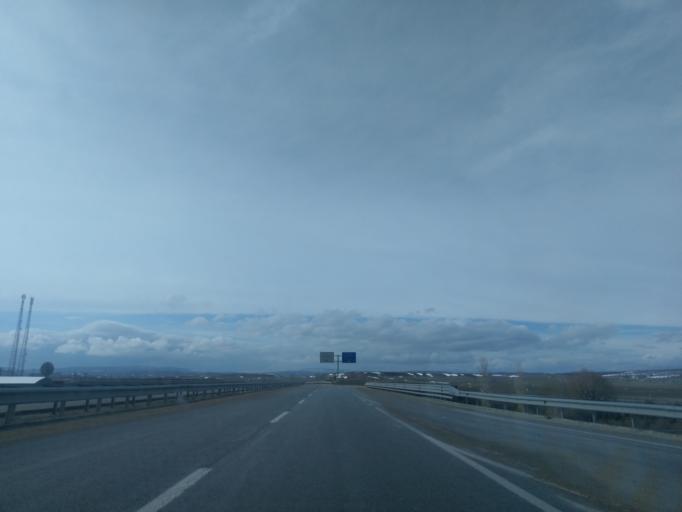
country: TR
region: Eskisehir
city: Inonu
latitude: 39.7086
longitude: 30.1582
